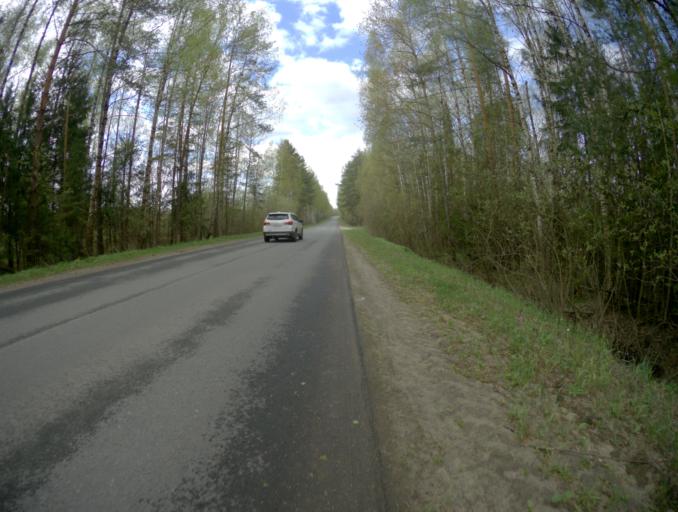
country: RU
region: Vladimir
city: Golovino
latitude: 55.9631
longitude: 40.5217
